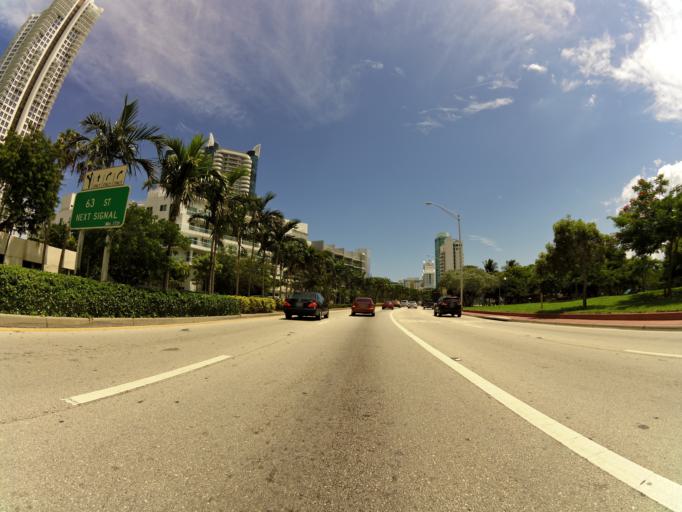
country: US
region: Florida
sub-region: Miami-Dade County
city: Surfside
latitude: 25.8463
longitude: -80.1212
